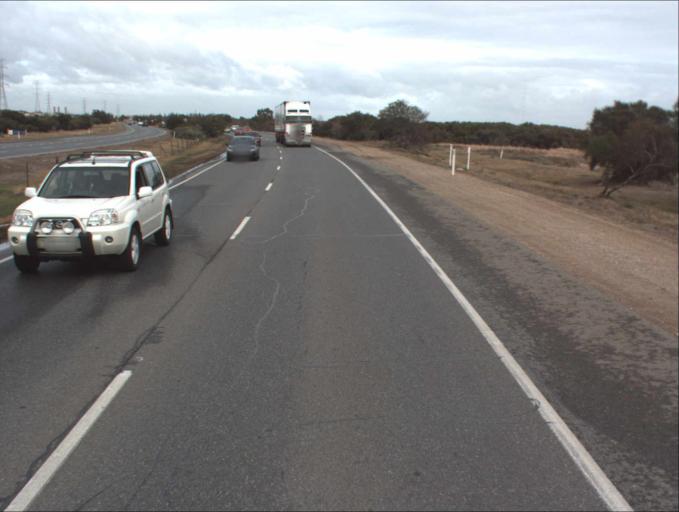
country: AU
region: South Australia
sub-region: Port Adelaide Enfield
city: Enfield
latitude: -34.8220
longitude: 138.5878
